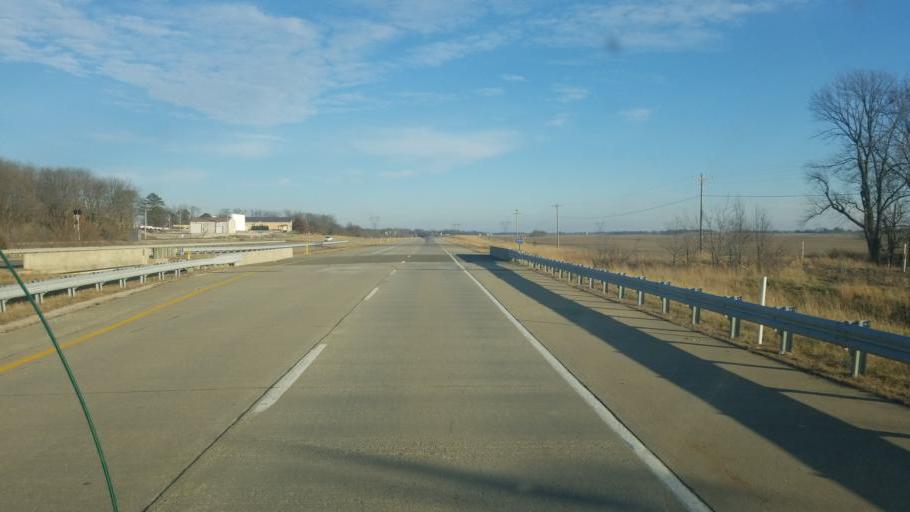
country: US
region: Indiana
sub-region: Knox County
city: Bicknell
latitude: 38.6710
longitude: -87.3505
